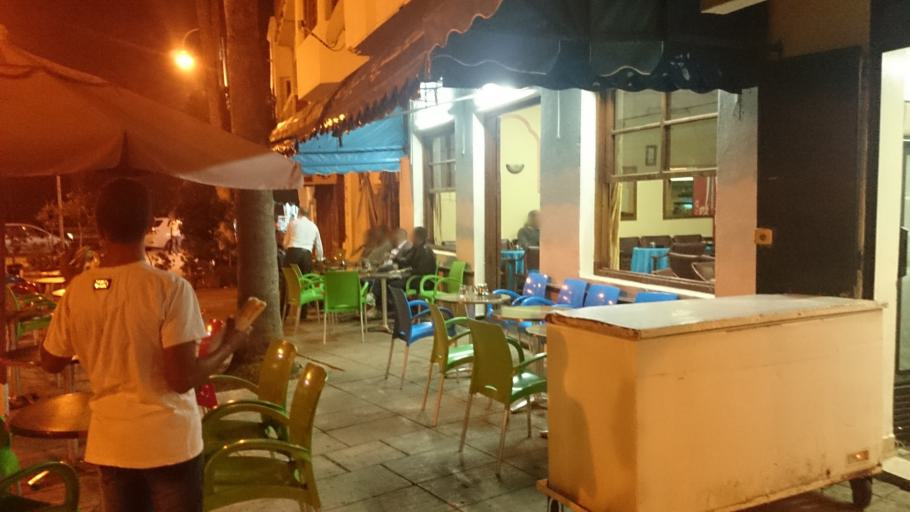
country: MA
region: Tanger-Tetouan
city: Asilah
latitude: 35.4665
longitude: -6.0355
